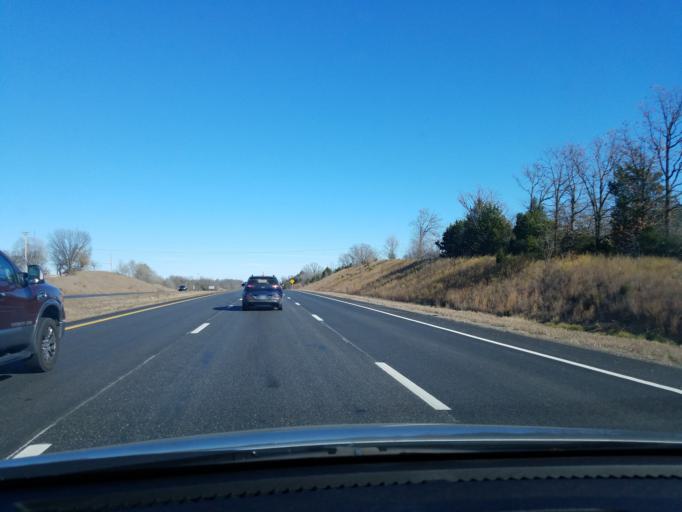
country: US
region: Missouri
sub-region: Taney County
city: Hollister
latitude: 36.5726
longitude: -93.2469
